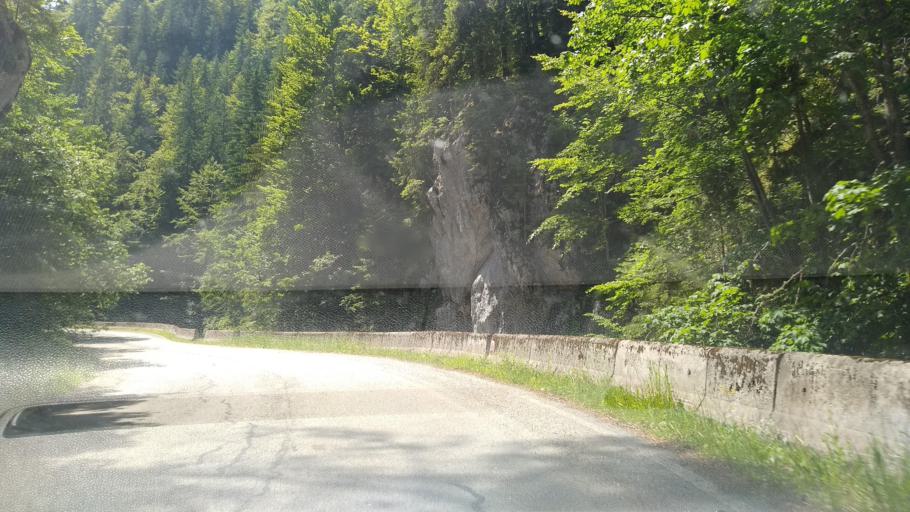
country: RO
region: Hunedoara
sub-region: Comuna Rau de Mori
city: Rau de Mori
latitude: 45.2767
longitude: 22.9073
